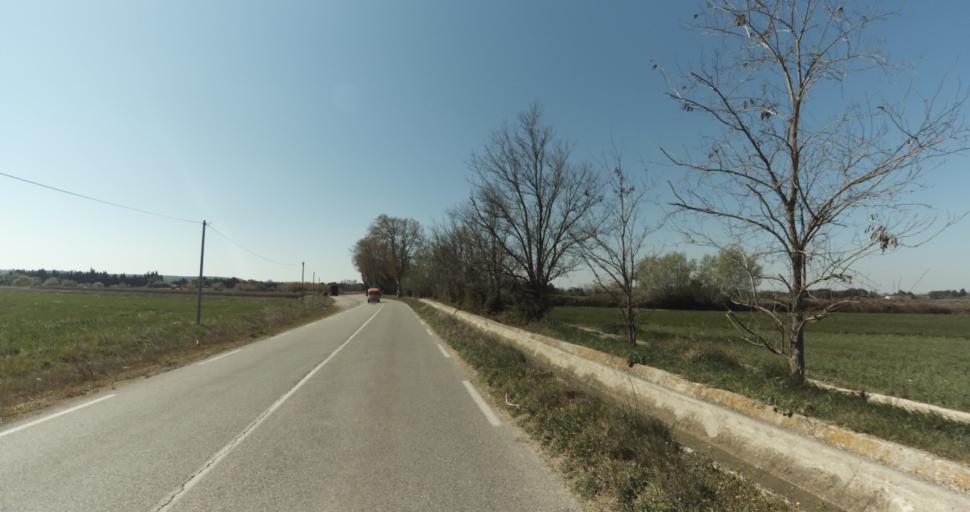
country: FR
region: Provence-Alpes-Cote d'Azur
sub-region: Departement des Bouches-du-Rhone
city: Pelissanne
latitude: 43.6235
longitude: 5.1458
